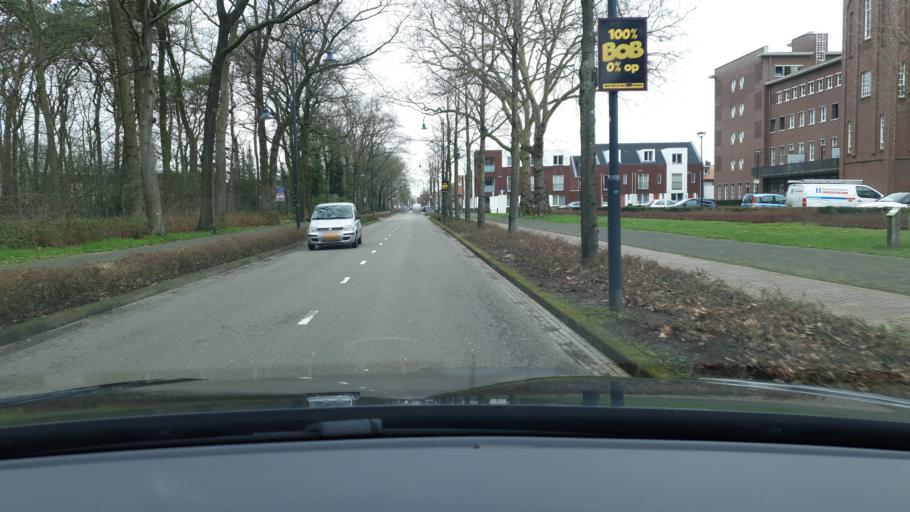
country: NL
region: North Brabant
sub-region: Gemeente Dongen
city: Dongen
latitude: 51.5795
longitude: 4.9251
